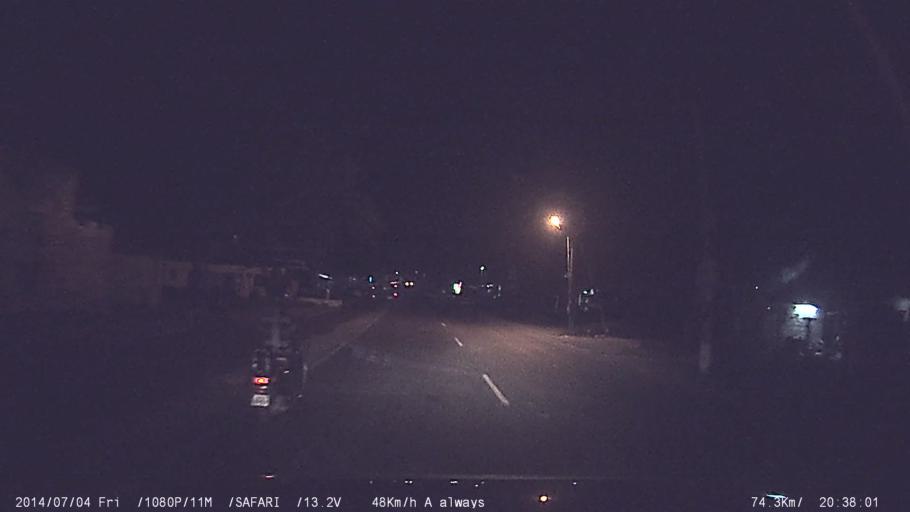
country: IN
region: Tamil Nadu
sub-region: Coimbatore
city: Madukkarai
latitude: 10.9025
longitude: 76.9415
